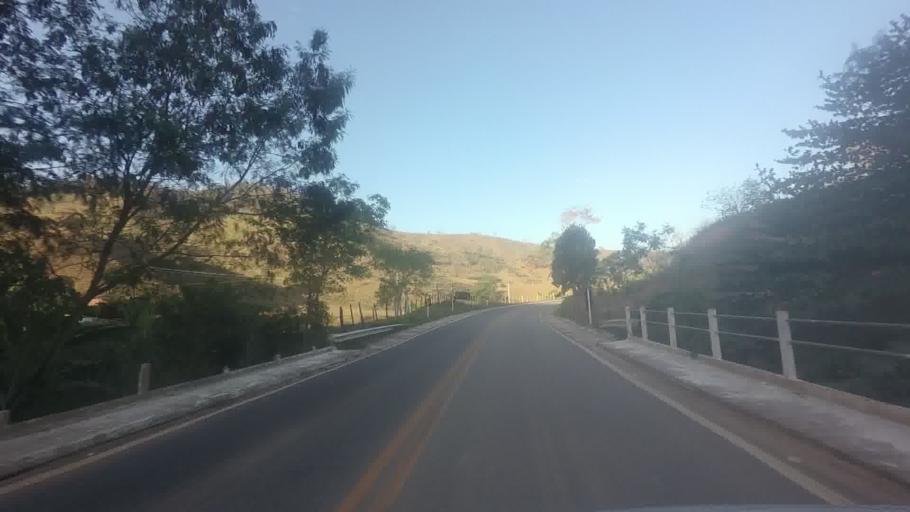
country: BR
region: Espirito Santo
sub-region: Cachoeiro De Itapemirim
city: Cachoeiro de Itapemirim
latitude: -20.8224
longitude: -41.2041
